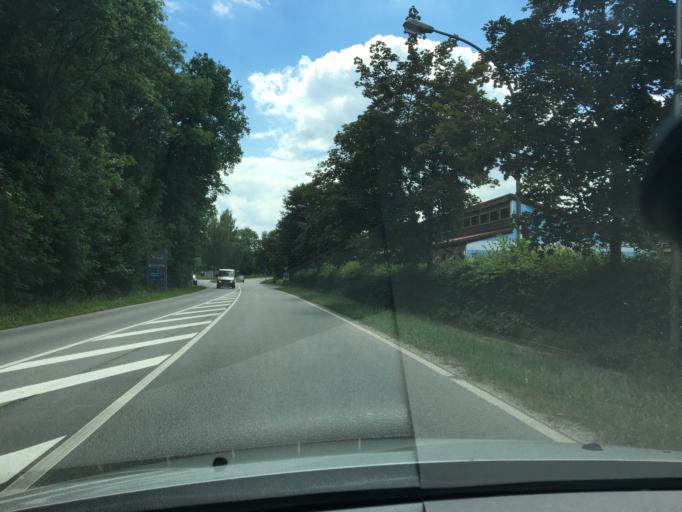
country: DE
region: Bavaria
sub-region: Lower Bavaria
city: Vilsbiburg
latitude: 48.4423
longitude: 12.3532
